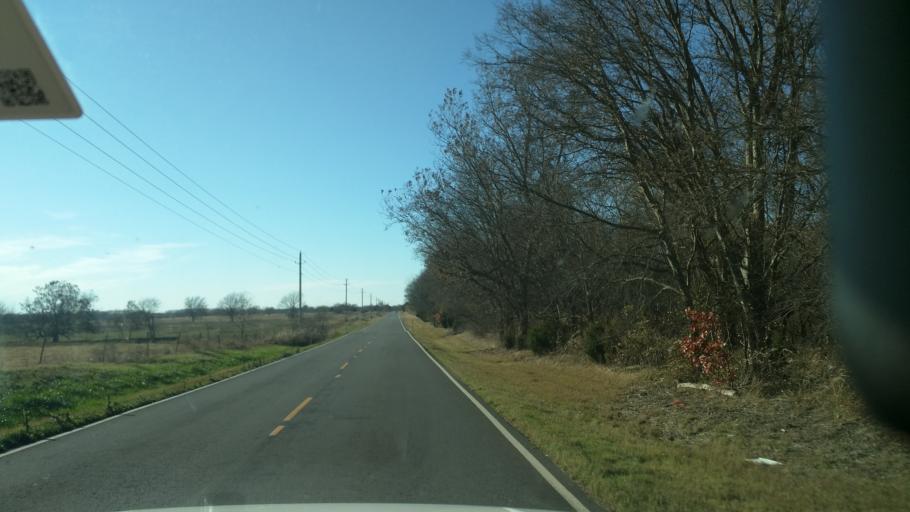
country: US
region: Oklahoma
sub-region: Nowata County
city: Nowata
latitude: 36.7716
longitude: -95.5820
